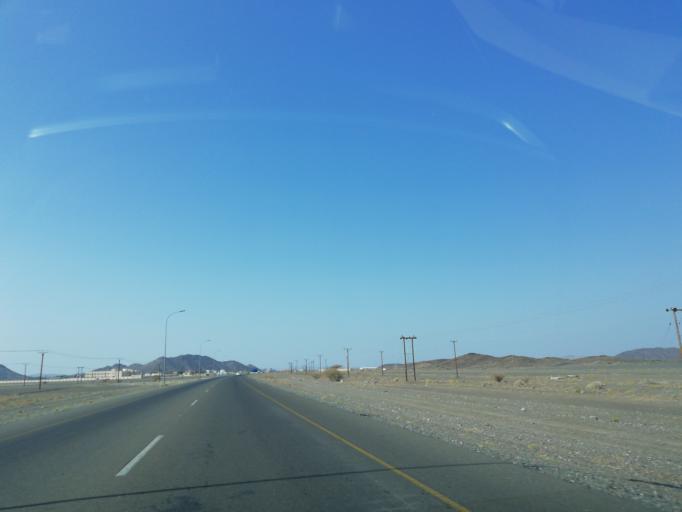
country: OM
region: Ash Sharqiyah
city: Ibra'
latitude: 22.7308
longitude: 58.1505
